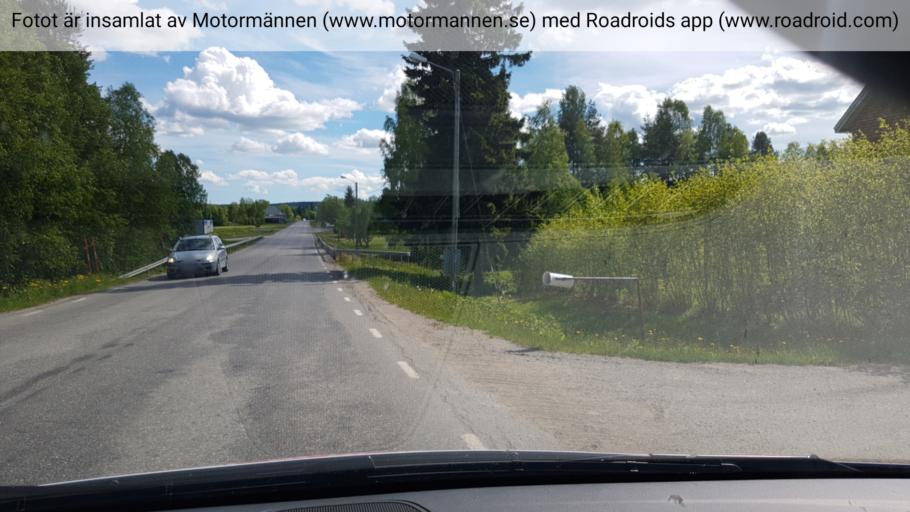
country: SE
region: Vaesterbotten
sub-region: Skelleftea Kommun
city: Forsbacka
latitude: 64.6867
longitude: 20.6016
